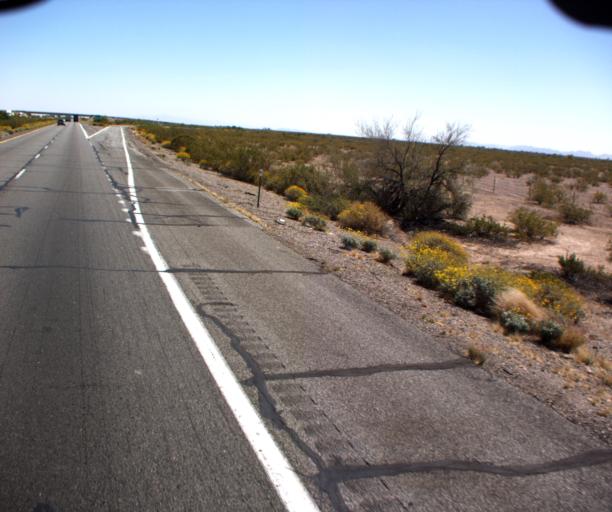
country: US
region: Arizona
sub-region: Maricopa County
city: Buckeye
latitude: 33.4835
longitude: -112.8756
